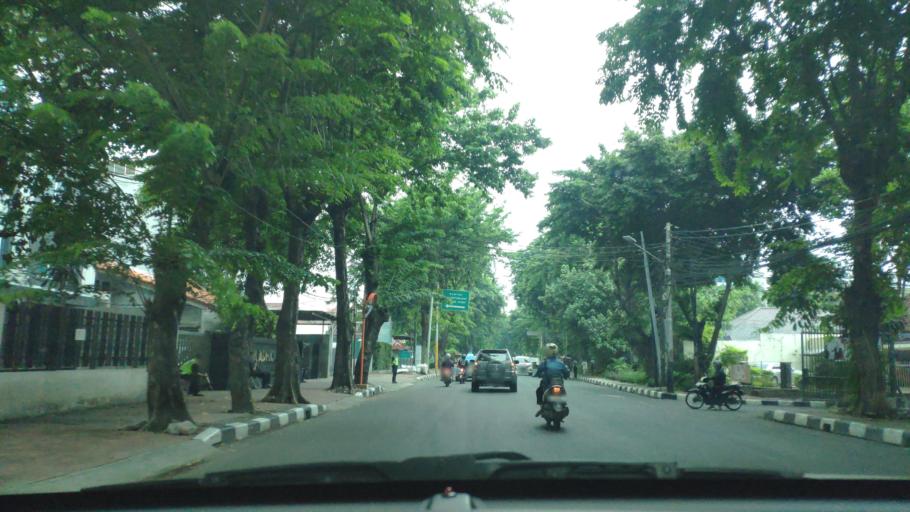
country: ID
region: Jakarta Raya
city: Jakarta
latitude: -6.1721
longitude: 106.8153
